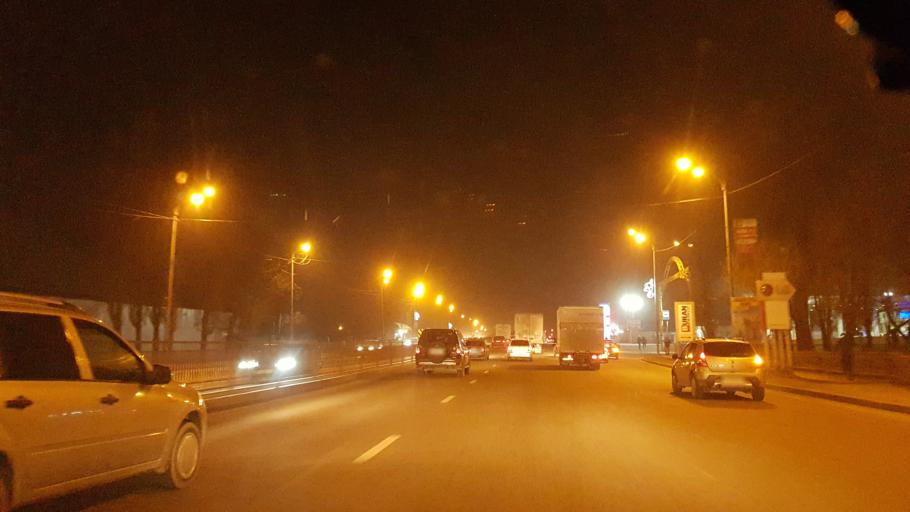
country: KZ
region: Almaty Qalasy
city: Almaty
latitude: 43.2647
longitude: 76.8643
